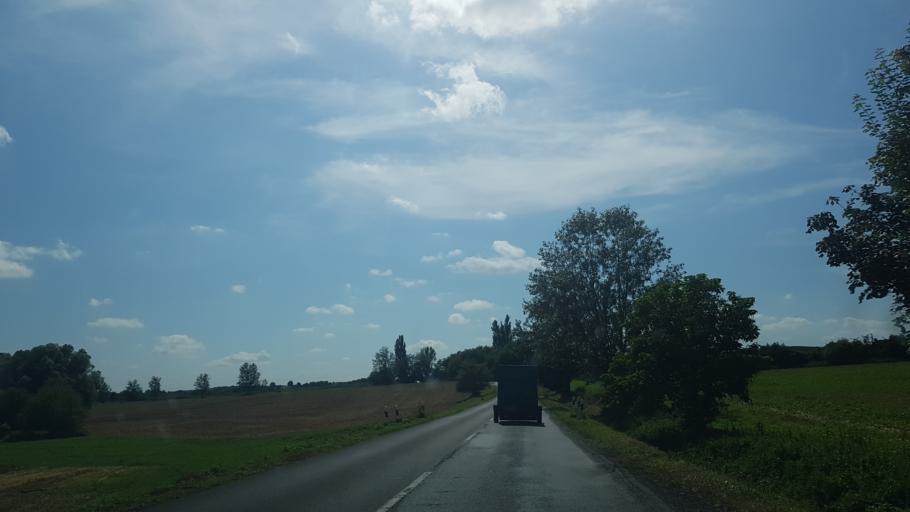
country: HU
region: Somogy
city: Bohonye
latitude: 46.4672
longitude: 17.3781
